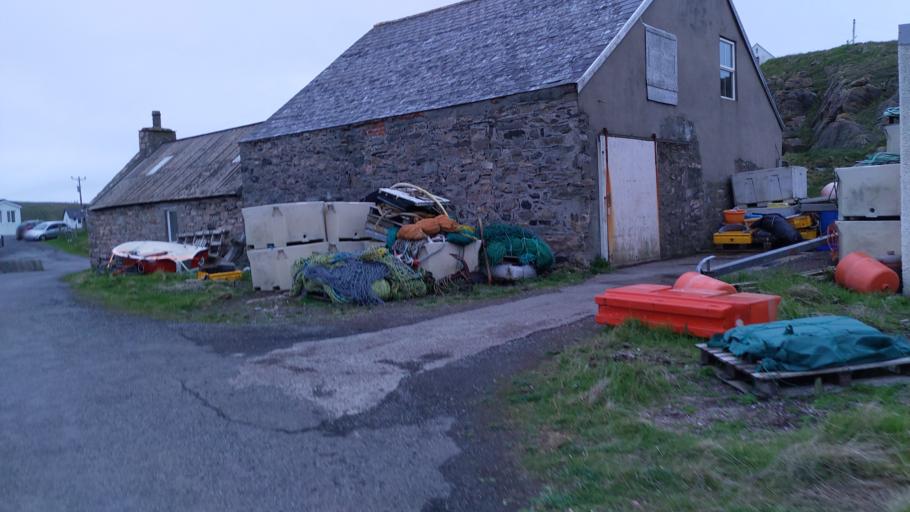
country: GB
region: Scotland
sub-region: Shetland Islands
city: Shetland
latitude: 60.4232
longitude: -0.7505
